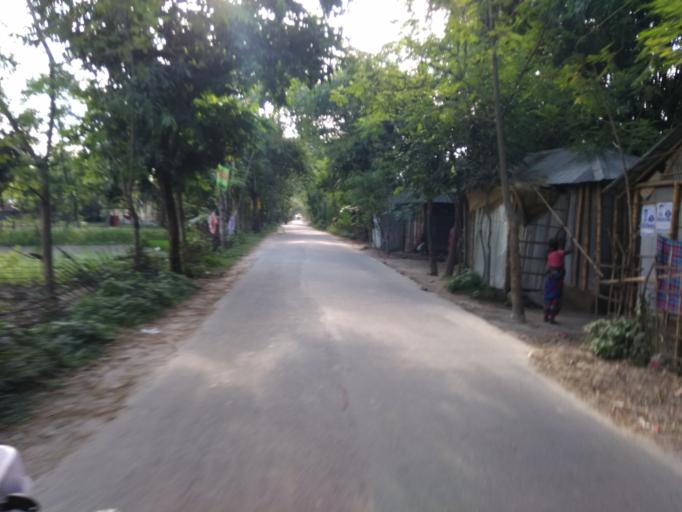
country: BD
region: Rangpur Division
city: Rangpur
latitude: 25.8302
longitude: 89.1192
